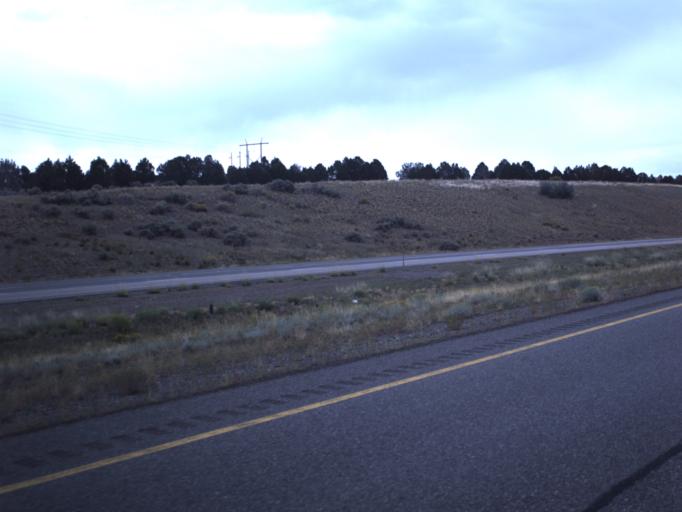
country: US
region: Utah
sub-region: Sevier County
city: Monroe
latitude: 38.5537
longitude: -112.4158
